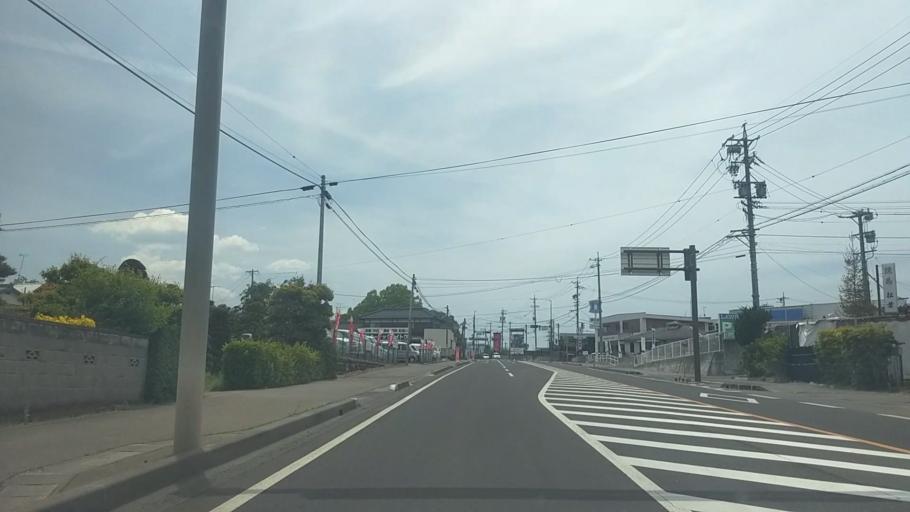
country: JP
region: Nagano
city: Saku
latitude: 36.1904
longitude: 138.4802
